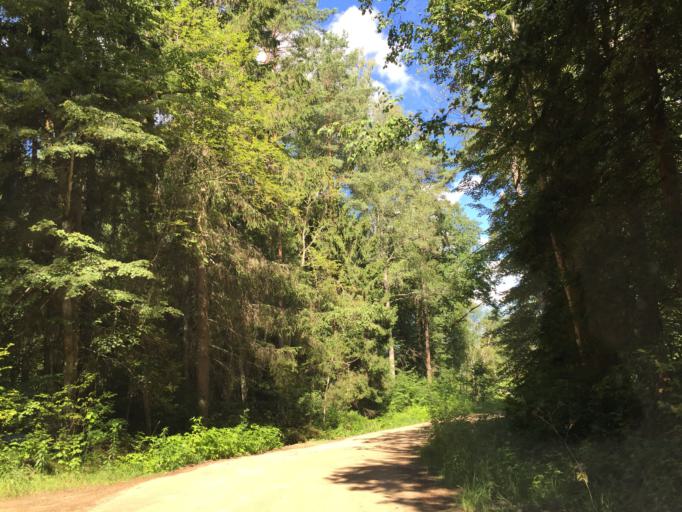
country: LV
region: Garkalne
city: Garkalne
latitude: 56.9756
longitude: 24.4547
